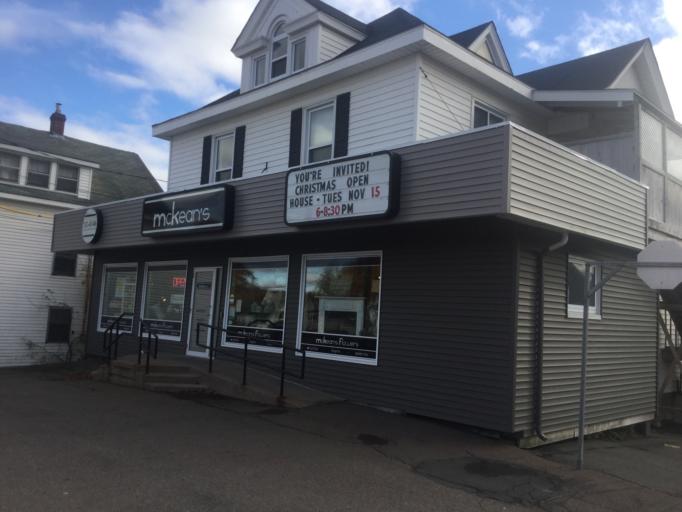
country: CA
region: Nova Scotia
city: New Glasgow
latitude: 45.5900
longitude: -62.6491
